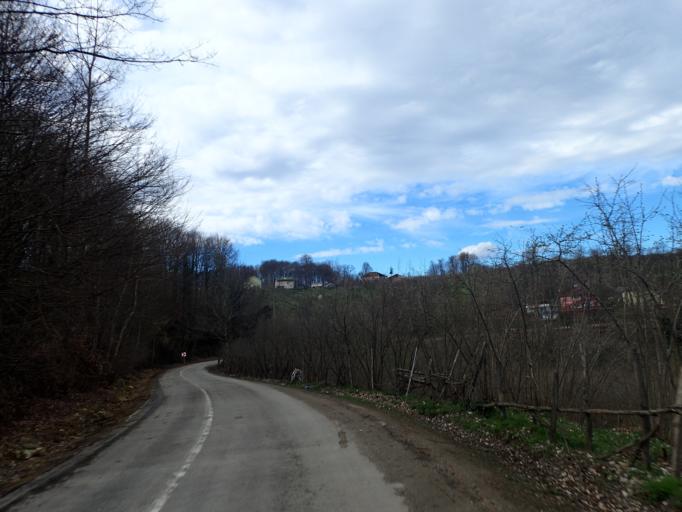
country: TR
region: Ordu
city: Kumru
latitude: 40.9377
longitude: 37.2638
